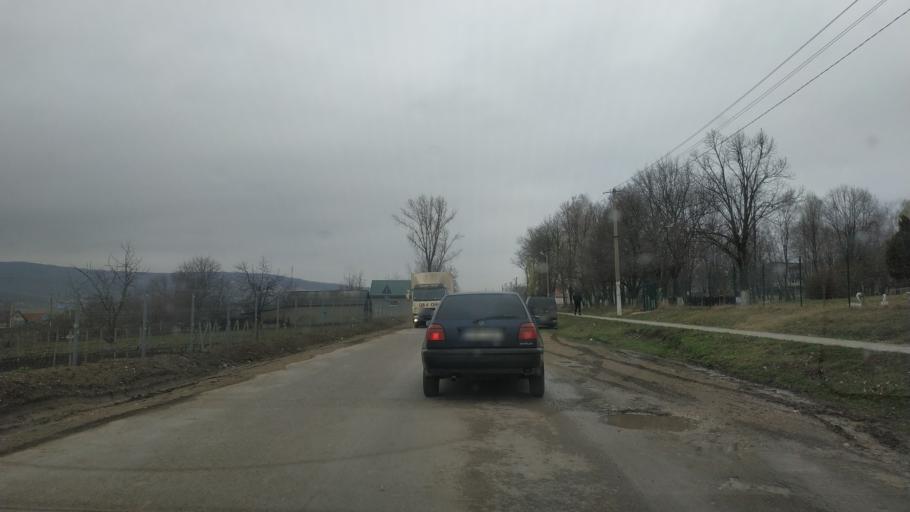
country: MD
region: Cantemir
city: Iargara
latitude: 46.3560
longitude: 28.3279
